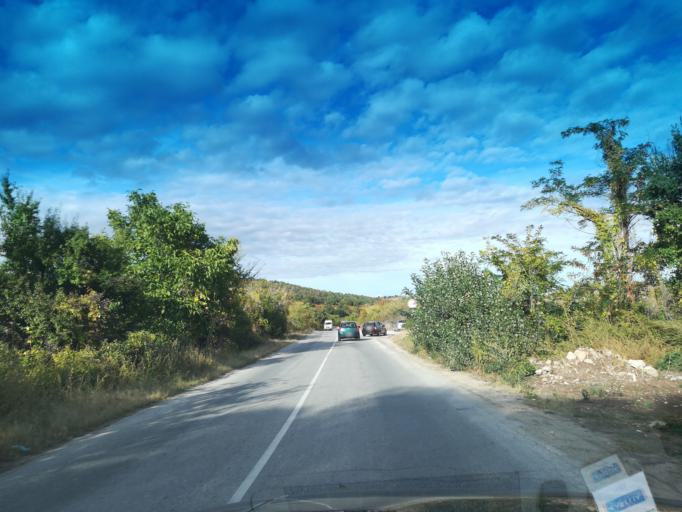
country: BG
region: Pazardzhik
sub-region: Obshtina Peshtera
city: Peshtera
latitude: 42.0473
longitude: 24.3101
